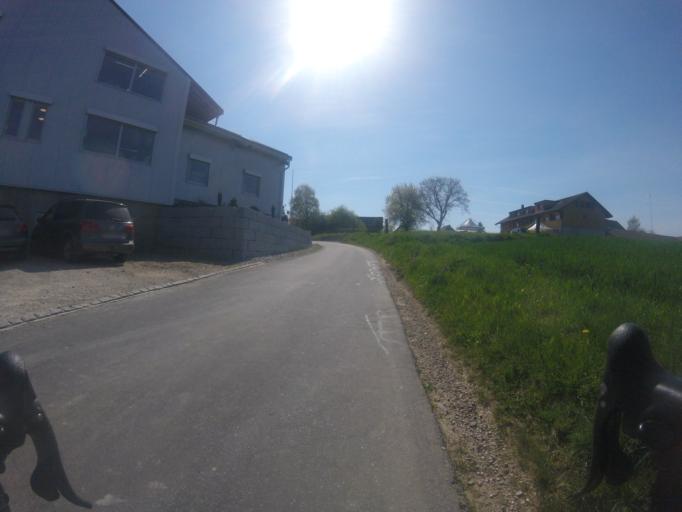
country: CH
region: Bern
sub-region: Bern-Mittelland District
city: Laupen
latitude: 46.9122
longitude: 7.2260
